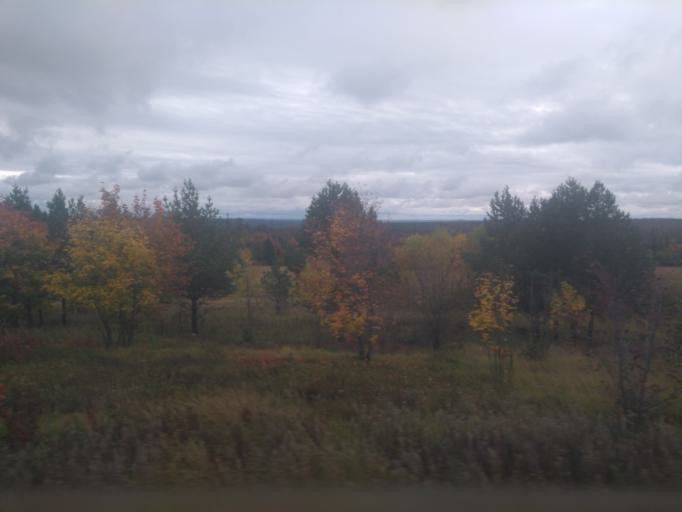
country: RU
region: Udmurtiya
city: Alnashi
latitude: 56.1550
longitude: 52.5839
